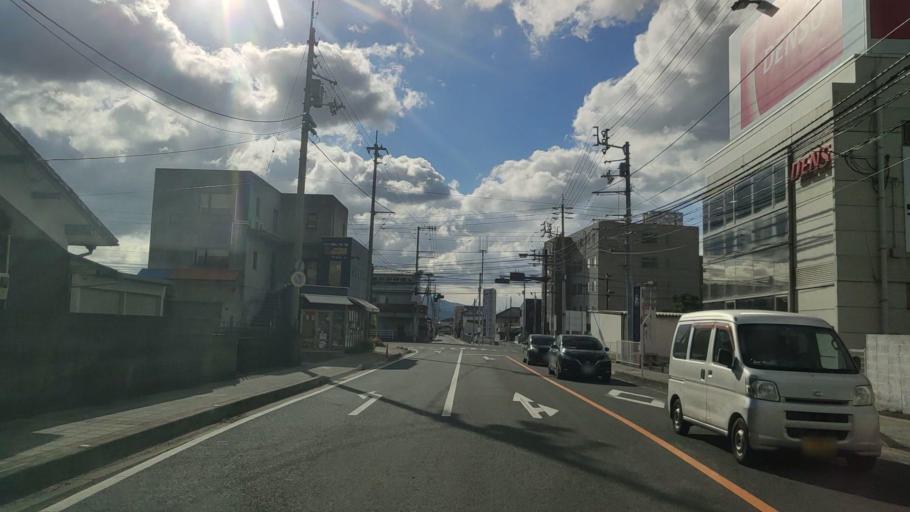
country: JP
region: Ehime
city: Masaki-cho
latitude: 33.8289
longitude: 132.7085
